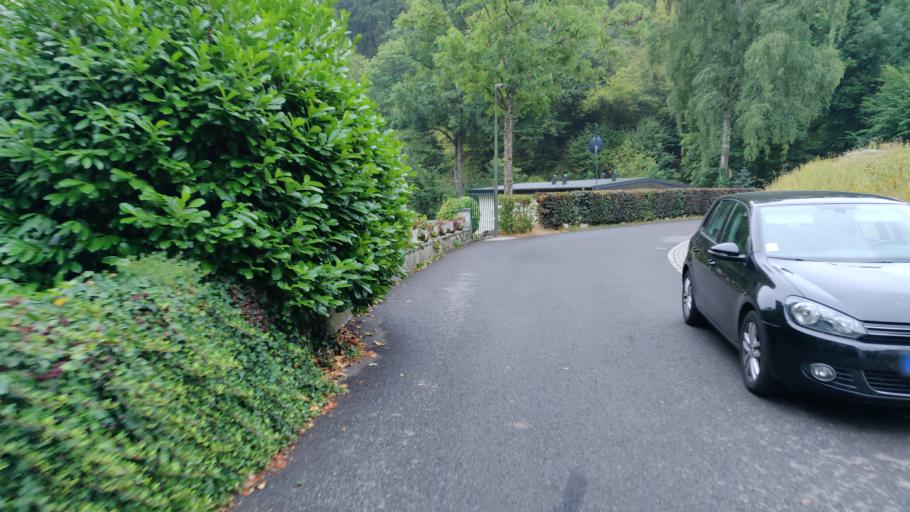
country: LU
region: Diekirch
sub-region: Canton de Wiltz
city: Goesdorf
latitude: 49.9052
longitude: 5.9622
